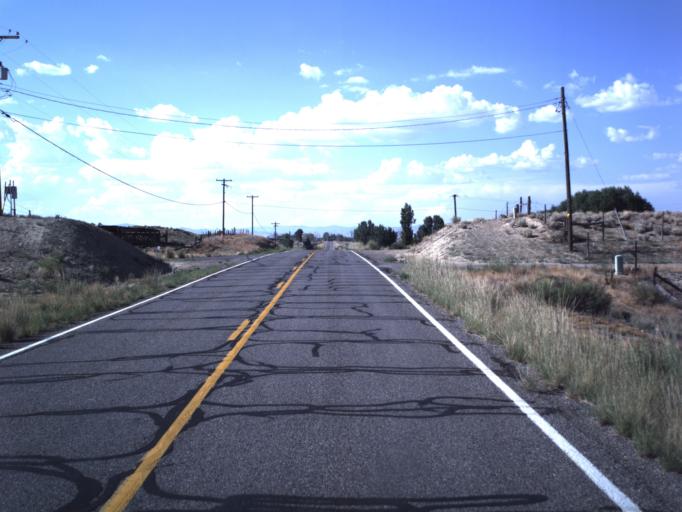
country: US
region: Utah
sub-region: Emery County
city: Huntington
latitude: 39.3944
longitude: -110.8525
